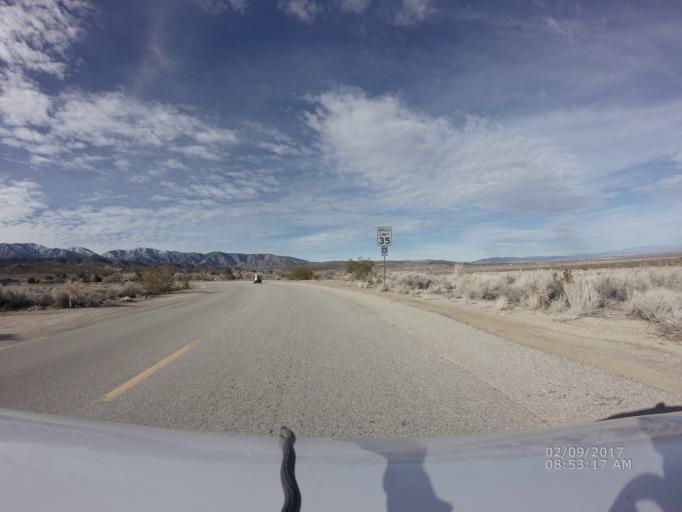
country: US
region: California
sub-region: Los Angeles County
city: Lake Los Angeles
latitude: 34.4781
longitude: -117.8359
